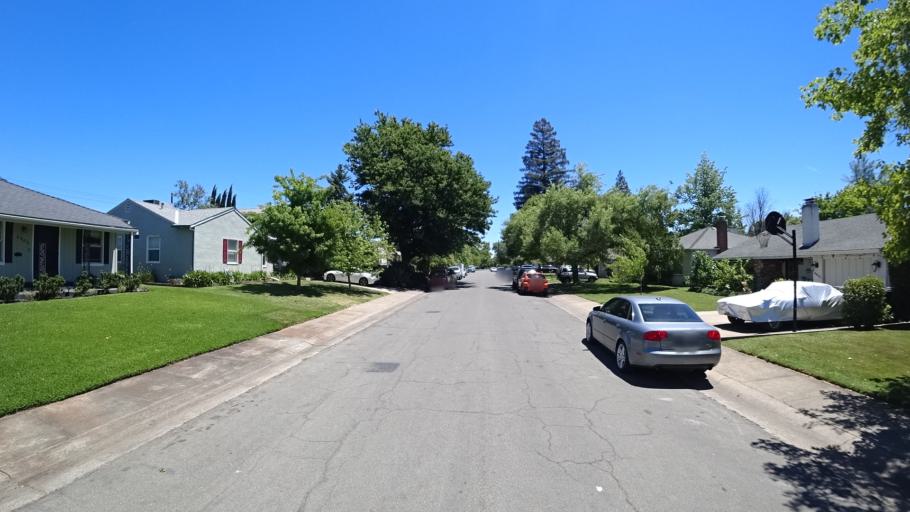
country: US
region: California
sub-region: Sacramento County
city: Sacramento
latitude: 38.5749
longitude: -121.4402
